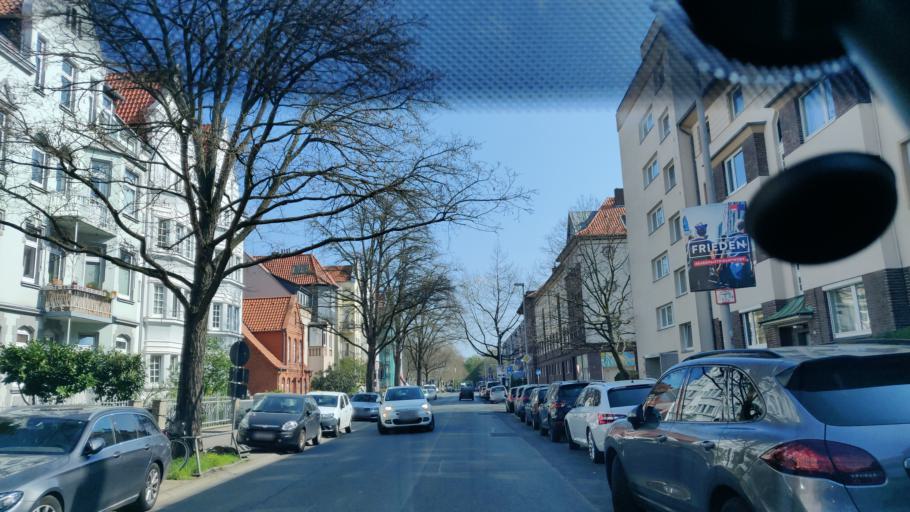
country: DE
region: Lower Saxony
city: Laatzen
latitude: 52.3375
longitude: 9.7664
